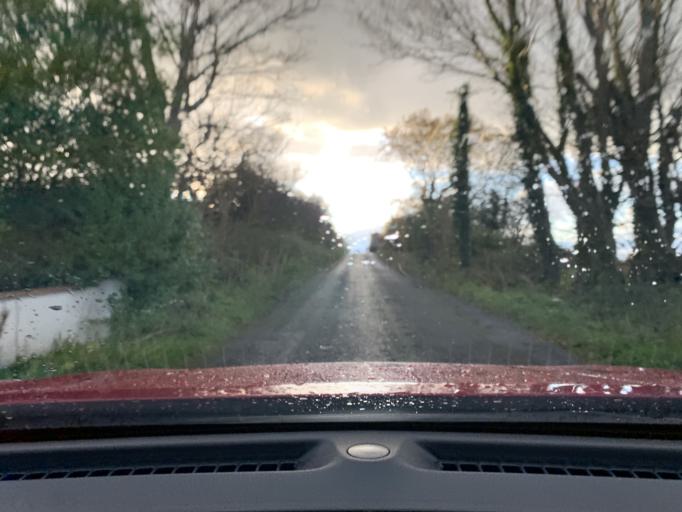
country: IE
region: Connaught
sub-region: Sligo
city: Sligo
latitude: 54.3119
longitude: -8.4947
